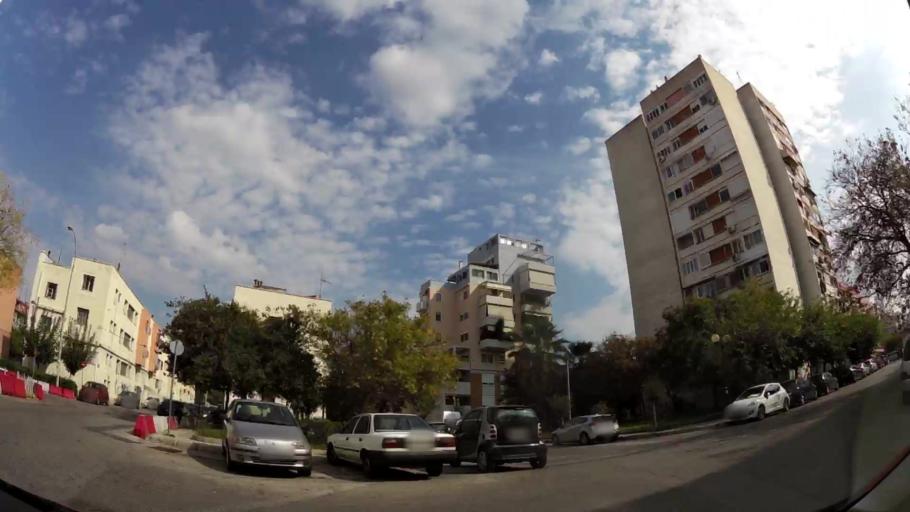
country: GR
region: Attica
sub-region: Nomarchia Athinas
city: Dhafni
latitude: 37.9592
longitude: 23.7222
